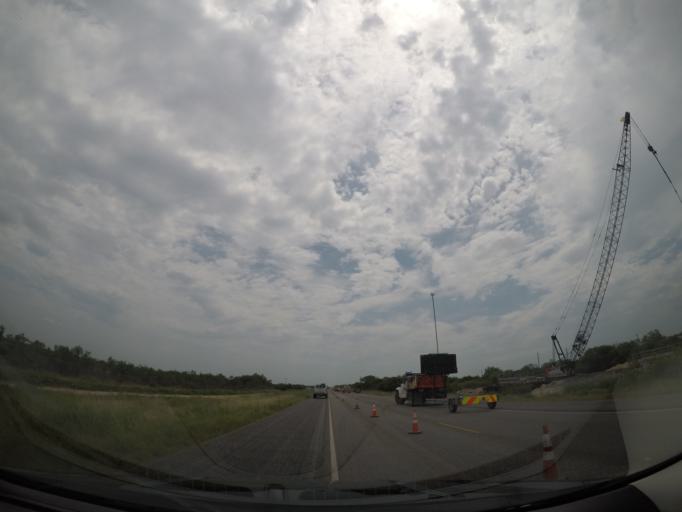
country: US
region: Texas
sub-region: Val Verde County
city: Laughlin Air Force Base
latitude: 29.3883
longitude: -100.7407
